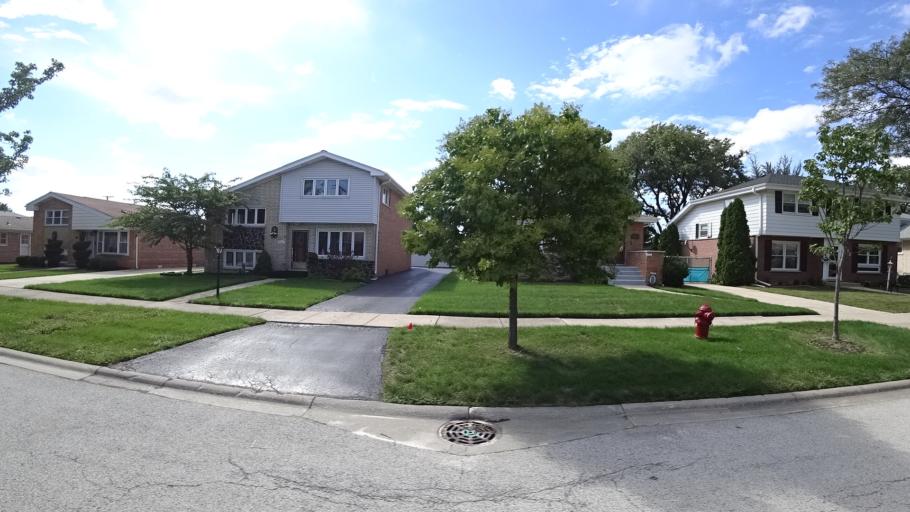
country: US
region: Illinois
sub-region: Cook County
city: Oak Lawn
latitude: 41.7207
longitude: -87.7640
